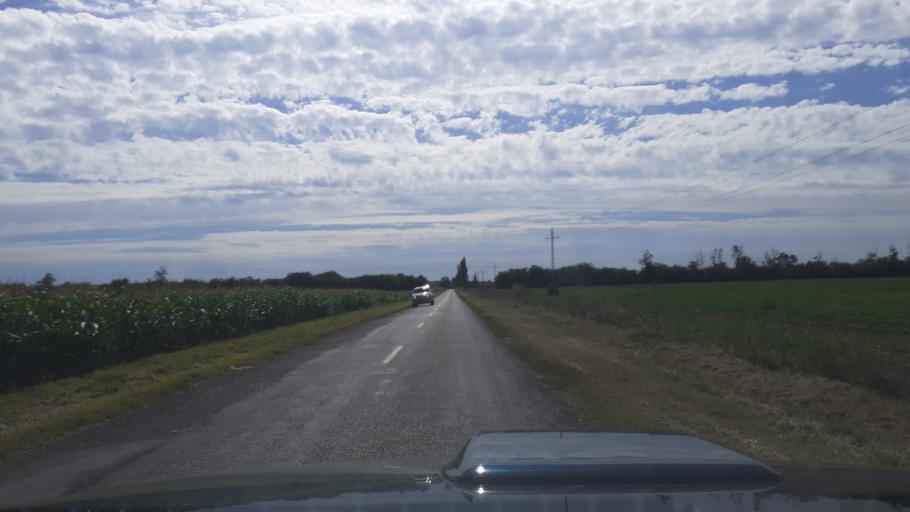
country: HU
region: Fejer
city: Pusztaszabolcs
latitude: 47.1248
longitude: 18.7716
